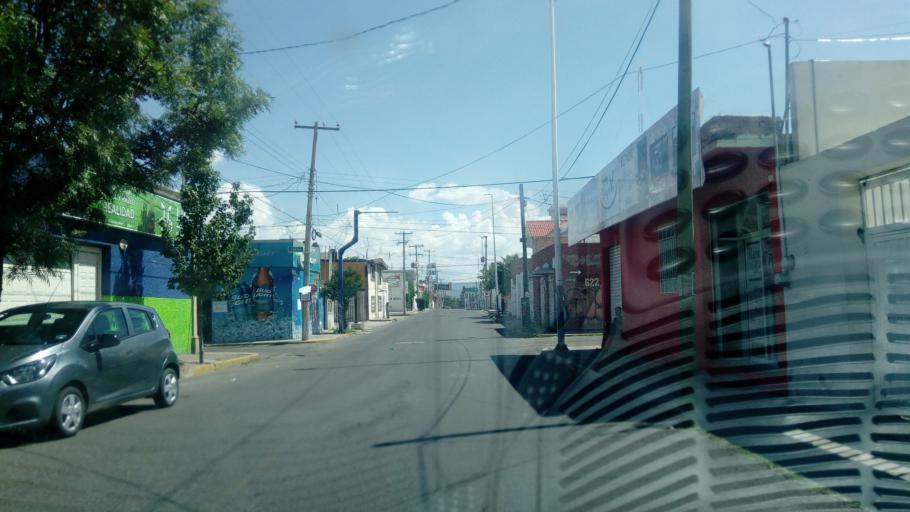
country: MX
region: Durango
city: Victoria de Durango
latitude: 24.0154
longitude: -104.6746
